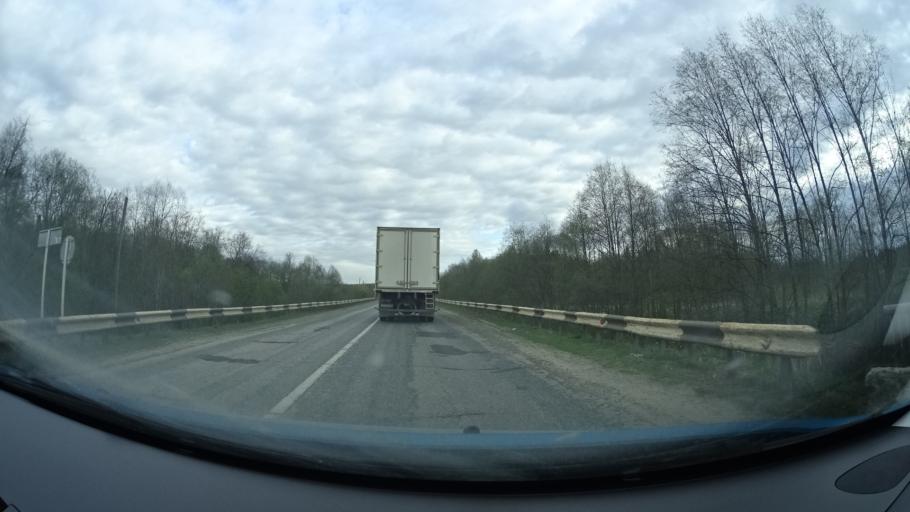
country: RU
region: Perm
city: Yugo-Kamskiy
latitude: 57.5438
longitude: 55.6847
